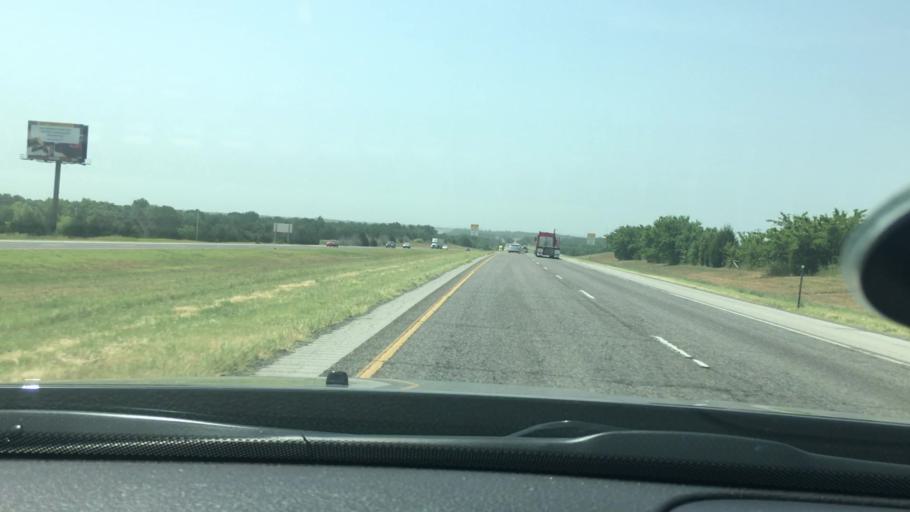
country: US
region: Oklahoma
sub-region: Garvin County
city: Wynnewood
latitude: 34.6115
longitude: -97.2131
